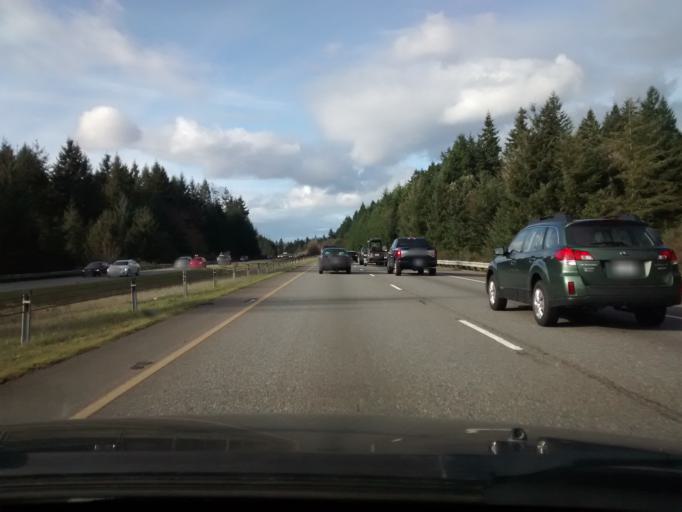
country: US
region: Washington
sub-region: Pierce County
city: Purdy
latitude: 47.3816
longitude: -122.6155
